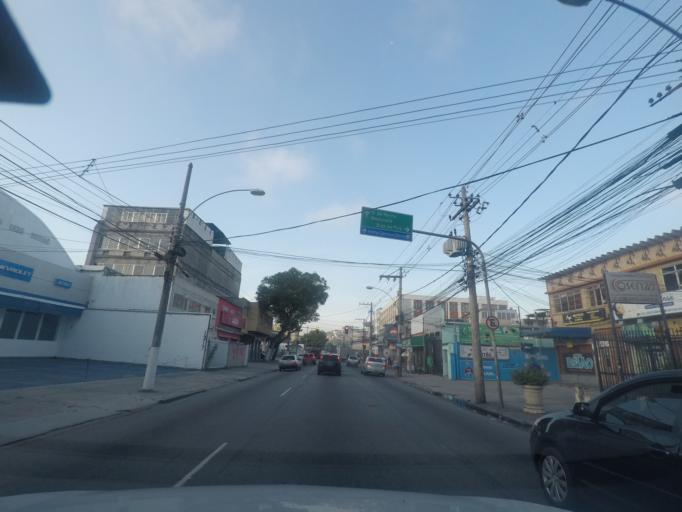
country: BR
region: Rio de Janeiro
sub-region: Duque De Caxias
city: Duque de Caxias
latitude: -22.8319
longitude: -43.2791
